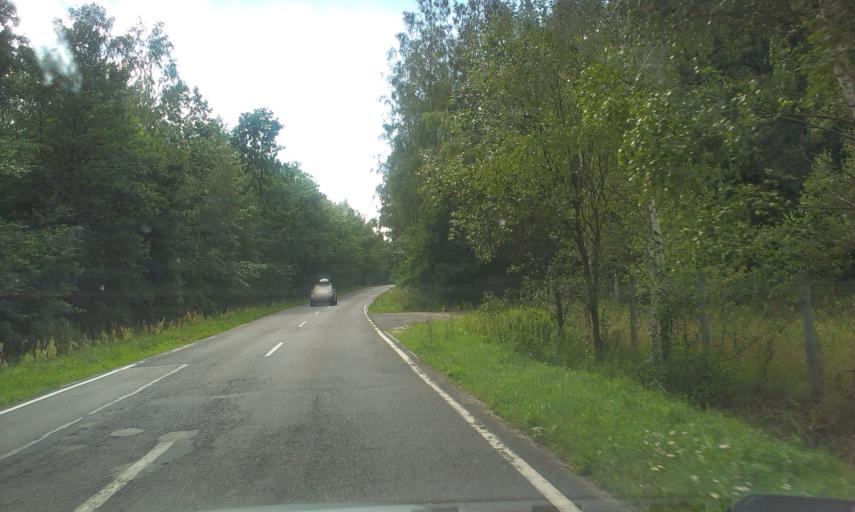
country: PL
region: Lodz Voivodeship
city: Zabia Wola
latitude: 51.9663
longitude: 20.6938
